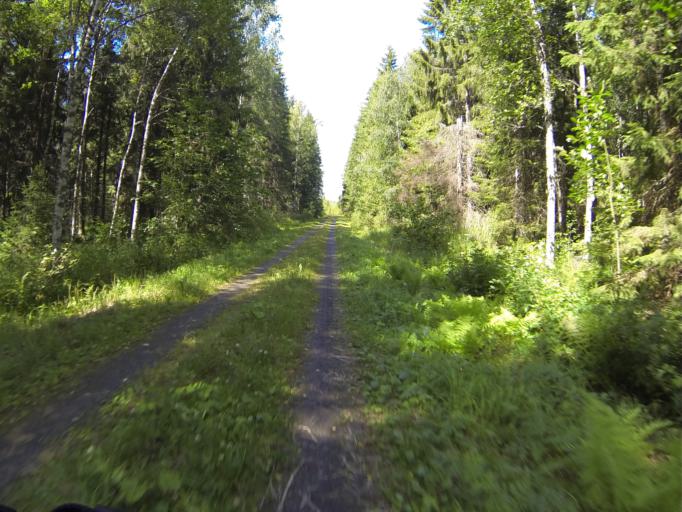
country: FI
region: Varsinais-Suomi
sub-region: Salo
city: Pernioe
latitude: 60.2790
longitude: 23.0586
